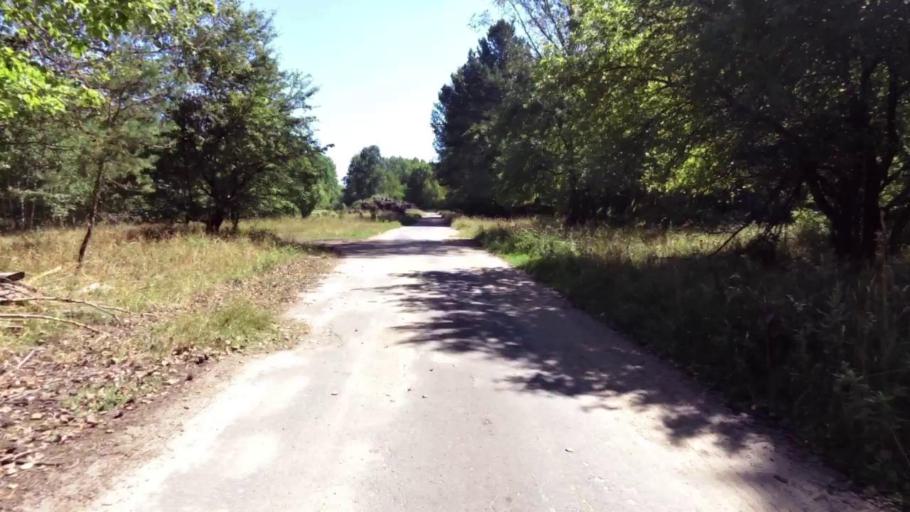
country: PL
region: West Pomeranian Voivodeship
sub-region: Powiat szczecinecki
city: Borne Sulinowo
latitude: 53.5933
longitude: 16.6460
